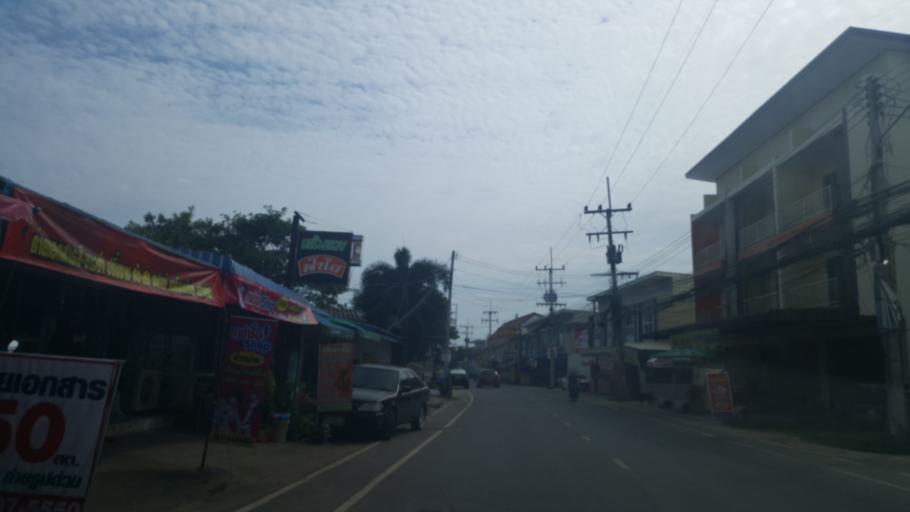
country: TH
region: Chon Buri
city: Sattahip
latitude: 12.6788
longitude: 100.9031
